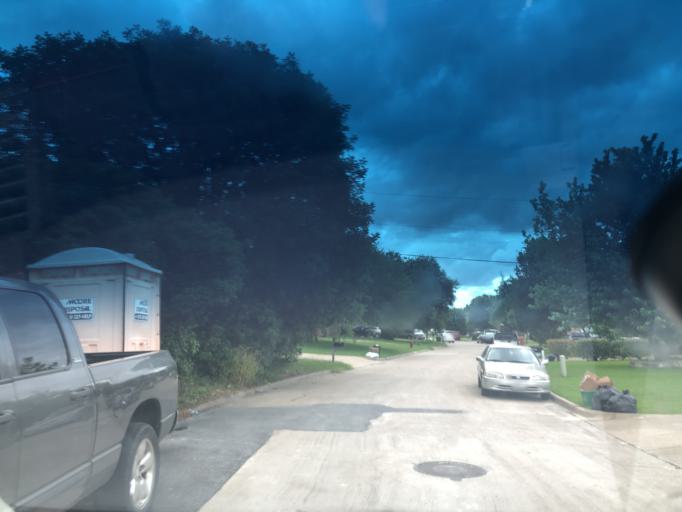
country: US
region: Texas
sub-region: Dallas County
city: Grand Prairie
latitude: 32.6938
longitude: -97.0127
